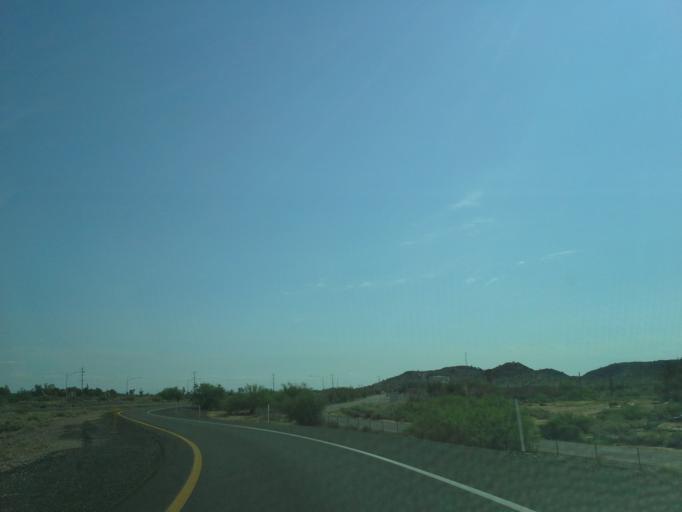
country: US
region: Arizona
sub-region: Pinal County
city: Casa Grande
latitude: 32.8275
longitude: -111.7393
